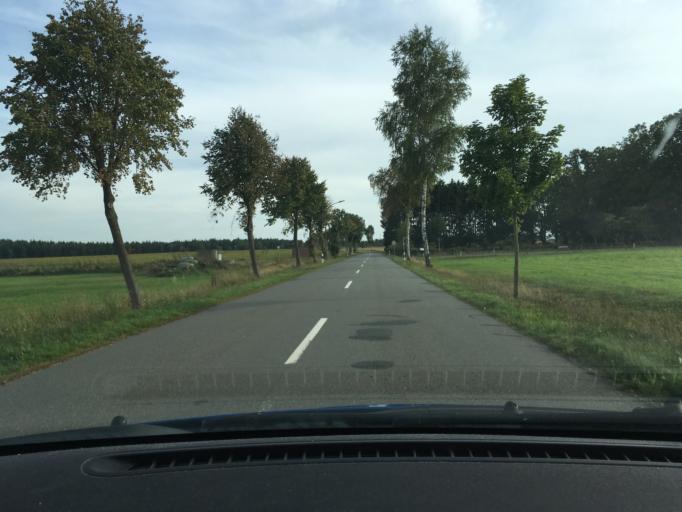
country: DE
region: Lower Saxony
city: Wietzendorf
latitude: 52.9141
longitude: 10.0512
